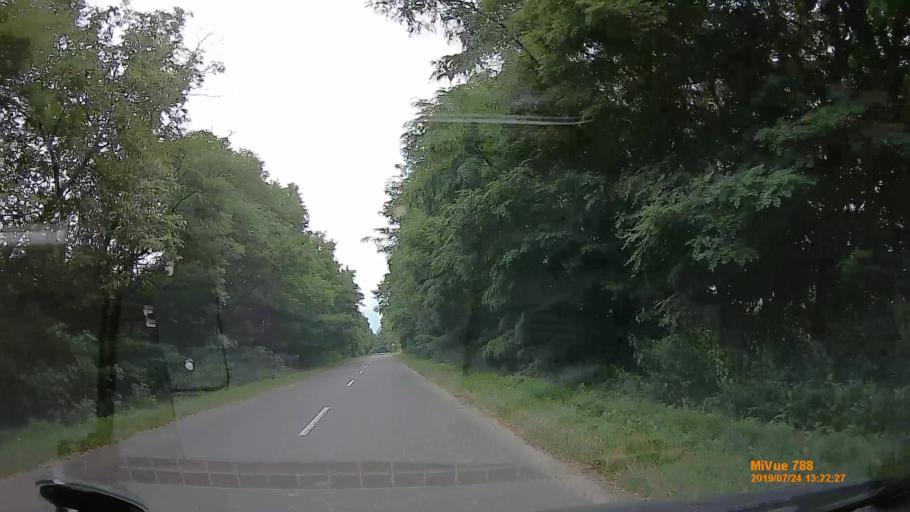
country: HU
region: Szabolcs-Szatmar-Bereg
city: Vasarosnameny
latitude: 48.2201
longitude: 22.4140
